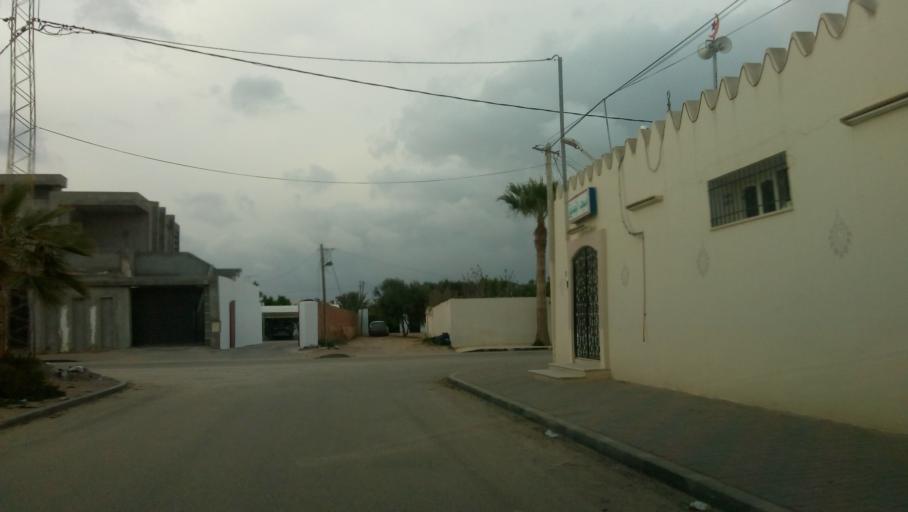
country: TN
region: Safaqis
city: Sfax
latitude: 34.7700
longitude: 10.7007
